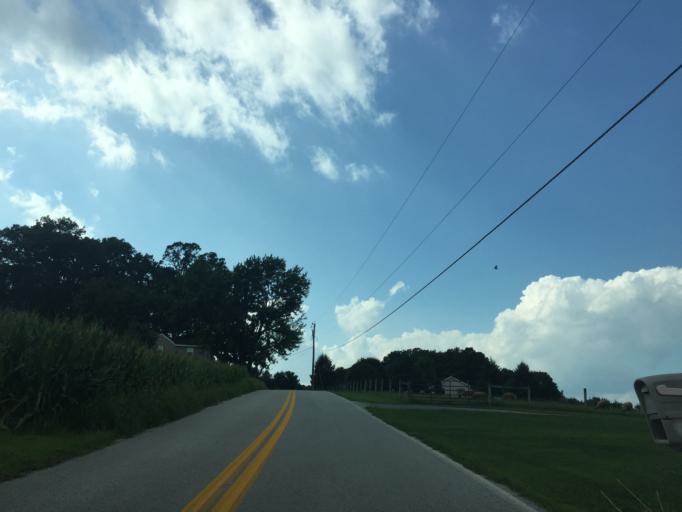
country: US
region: Maryland
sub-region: Carroll County
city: Manchester
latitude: 39.6278
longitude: -76.9035
